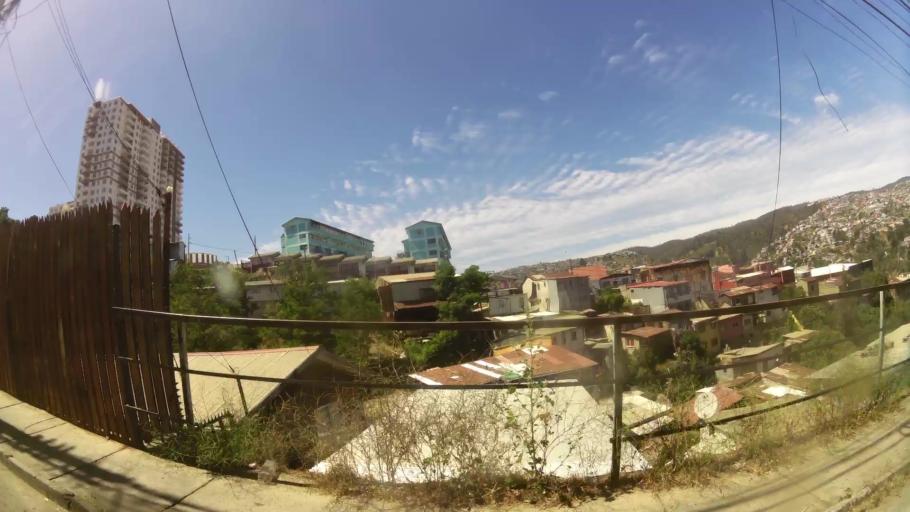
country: CL
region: Valparaiso
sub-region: Provincia de Valparaiso
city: Valparaiso
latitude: -33.0488
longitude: -71.5983
